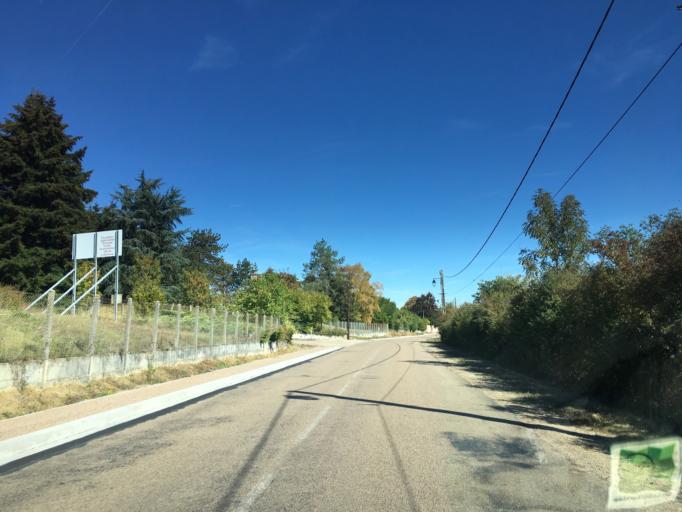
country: FR
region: Bourgogne
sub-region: Departement de l'Yonne
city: Vermenton
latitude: 47.6553
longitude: 3.6597
